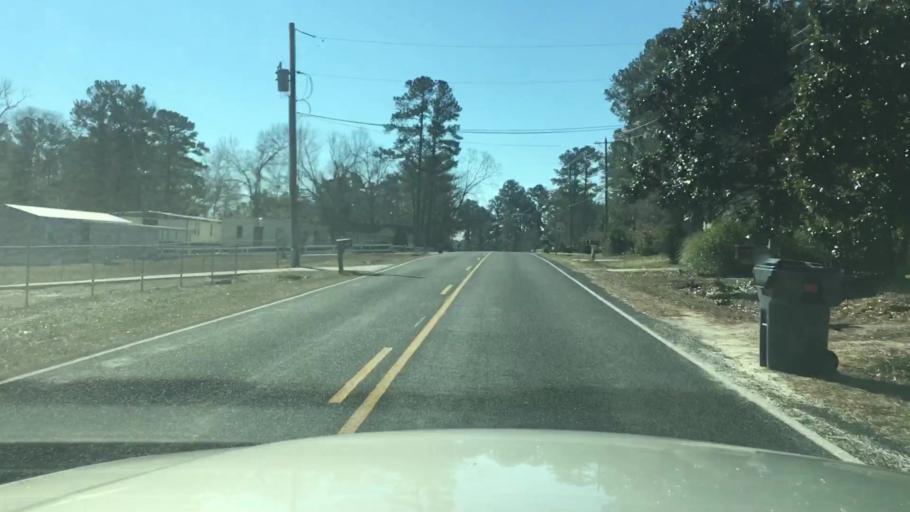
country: US
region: North Carolina
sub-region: Cumberland County
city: Hope Mills
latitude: 34.9991
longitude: -78.9650
